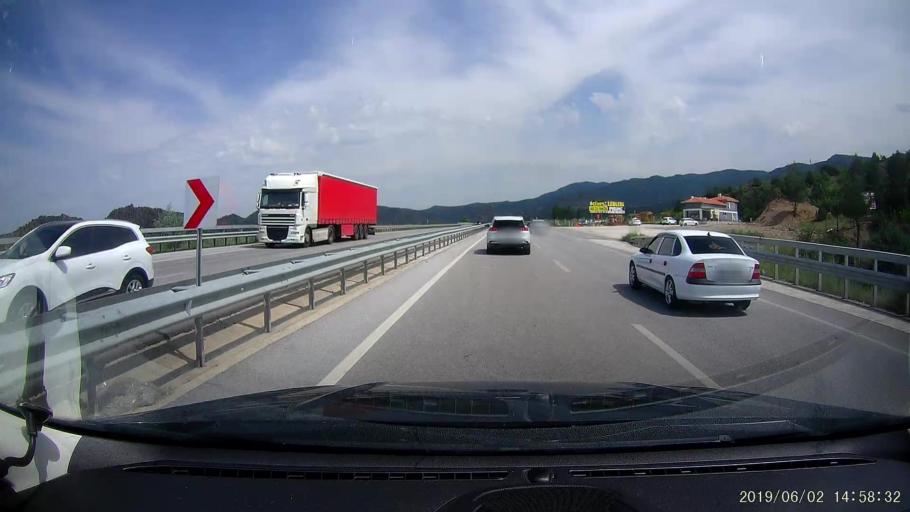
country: TR
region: Corum
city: Osmancik
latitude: 40.9806
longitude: 34.6786
